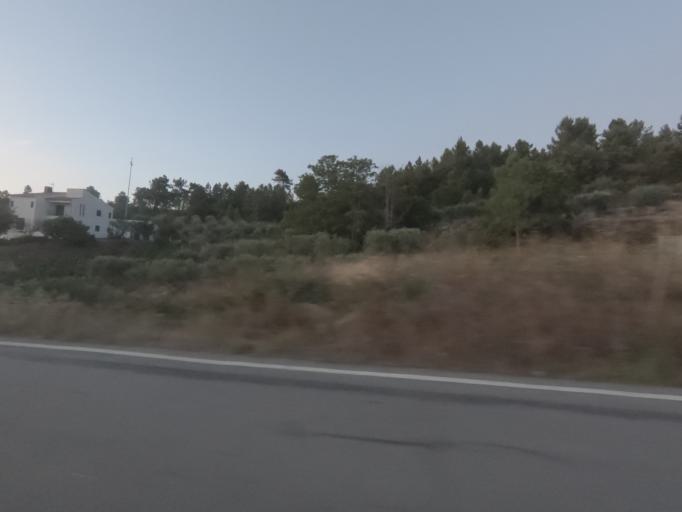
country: PT
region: Viseu
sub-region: Armamar
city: Armamar
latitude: 41.2005
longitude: -7.6975
